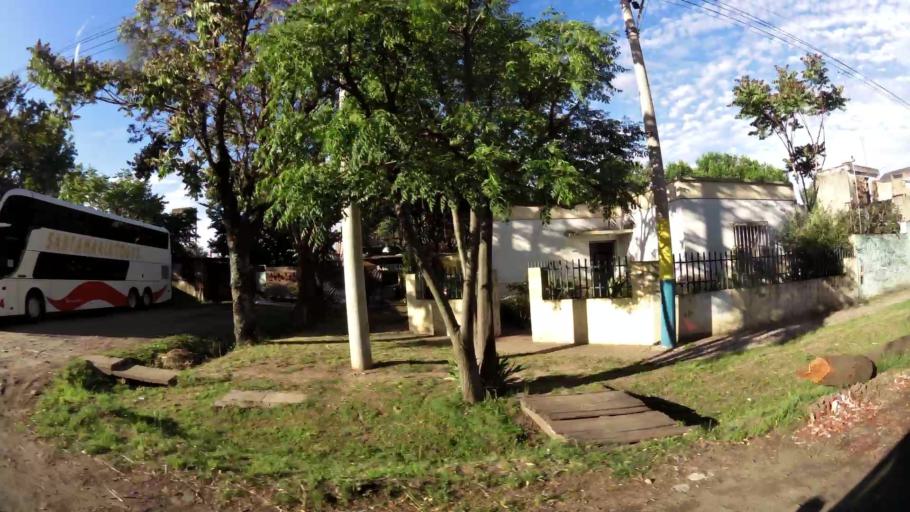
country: AR
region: Santa Fe
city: Gobernador Galvez
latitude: -32.9884
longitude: -60.6745
